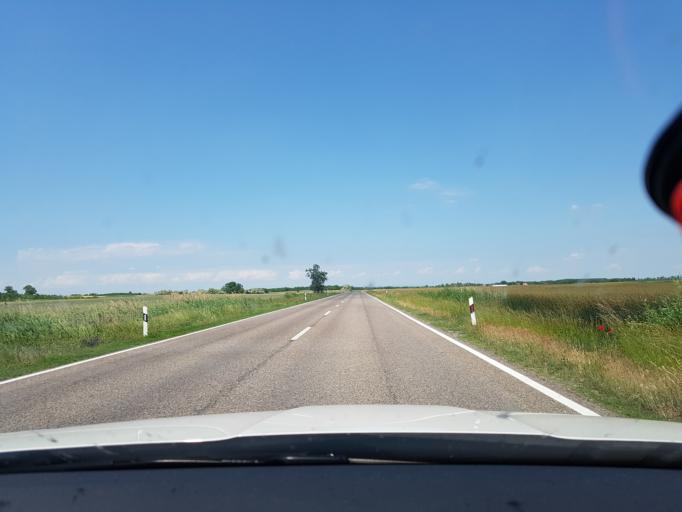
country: HU
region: Hajdu-Bihar
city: Egyek
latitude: 47.5750
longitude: 20.8573
